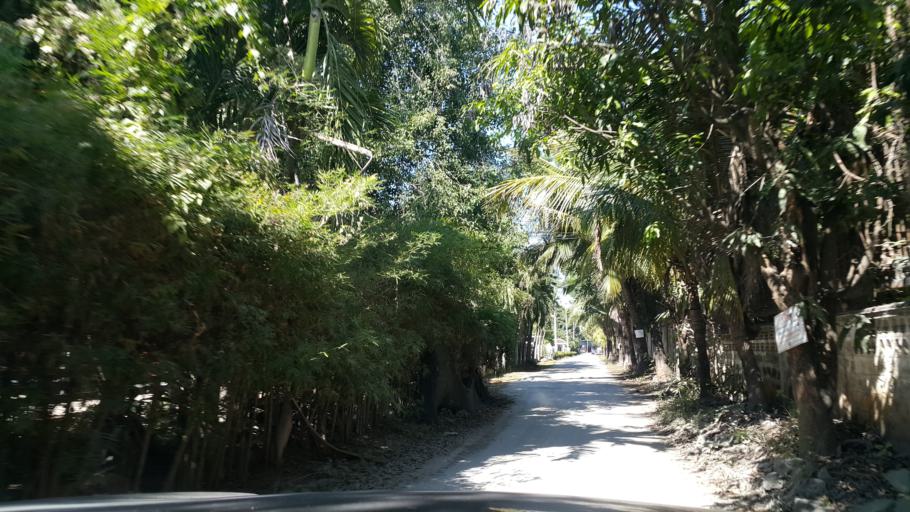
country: TH
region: Chiang Mai
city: Chiang Mai
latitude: 18.7808
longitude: 99.0297
